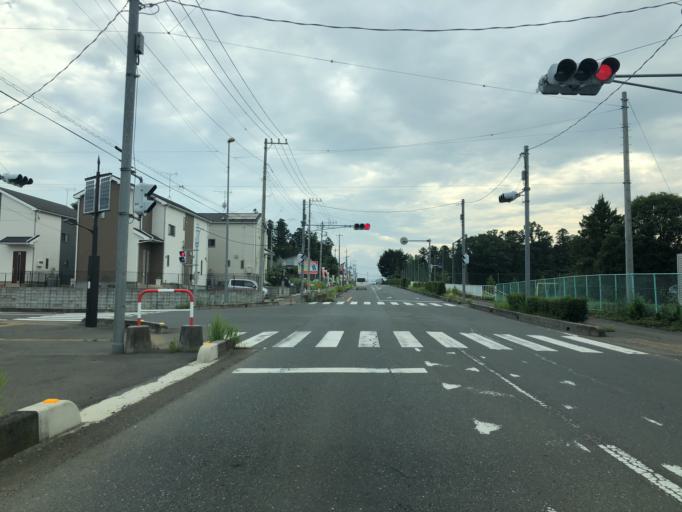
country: JP
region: Saitama
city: Fukiage-fujimi
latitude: 36.0512
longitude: 139.3996
